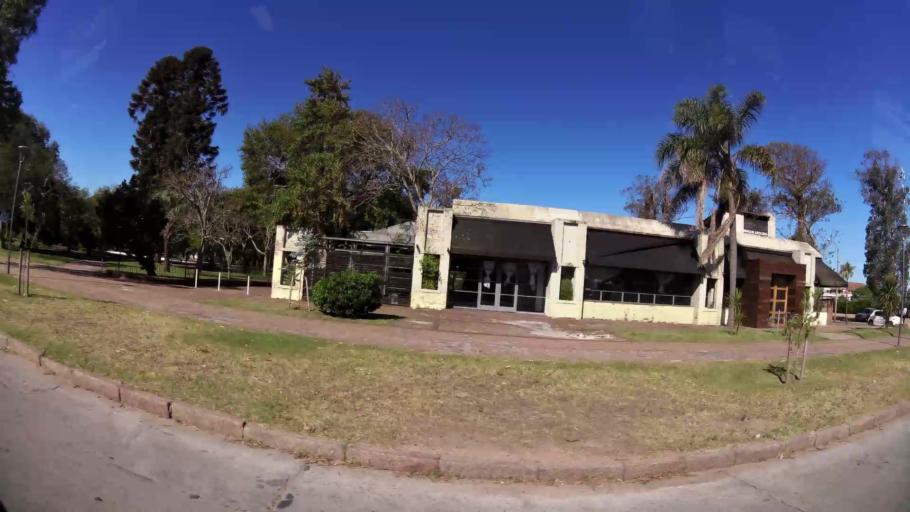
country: UY
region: Canelones
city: Paso de Carrasco
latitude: -34.8841
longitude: -56.0597
